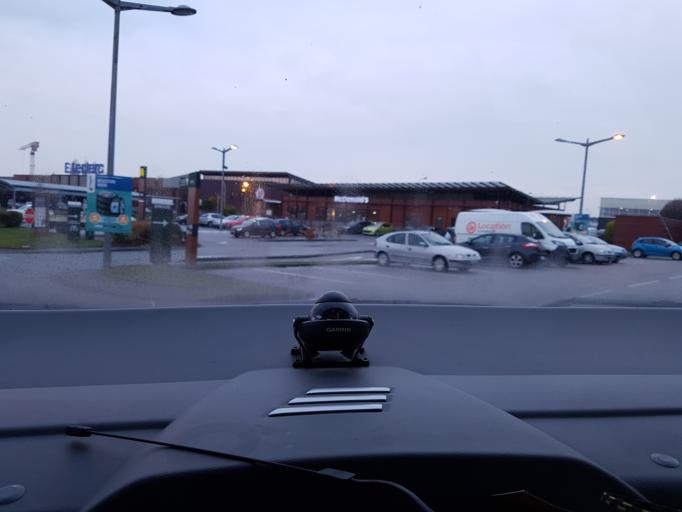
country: FR
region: Haute-Normandie
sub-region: Departement de la Seine-Maritime
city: Sainte-Marie-des-Champs
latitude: 49.6127
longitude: 0.7756
